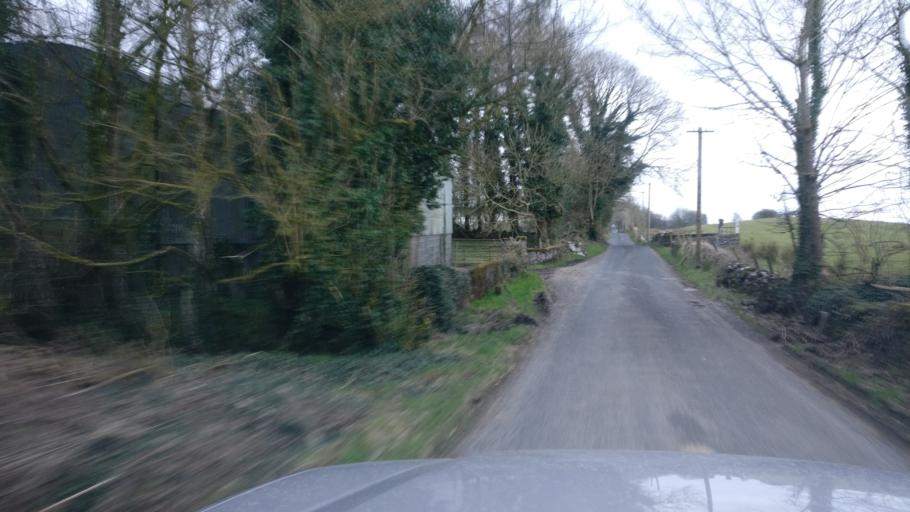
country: IE
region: Connaught
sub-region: County Galway
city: Loughrea
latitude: 53.2603
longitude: -8.4523
